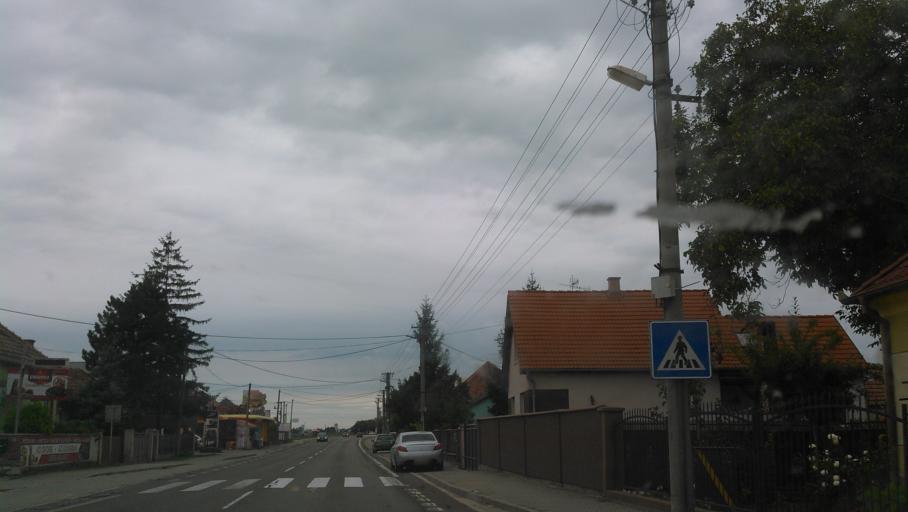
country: SK
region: Trnavsky
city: Dunajska Streda
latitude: 47.9777
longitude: 17.6592
